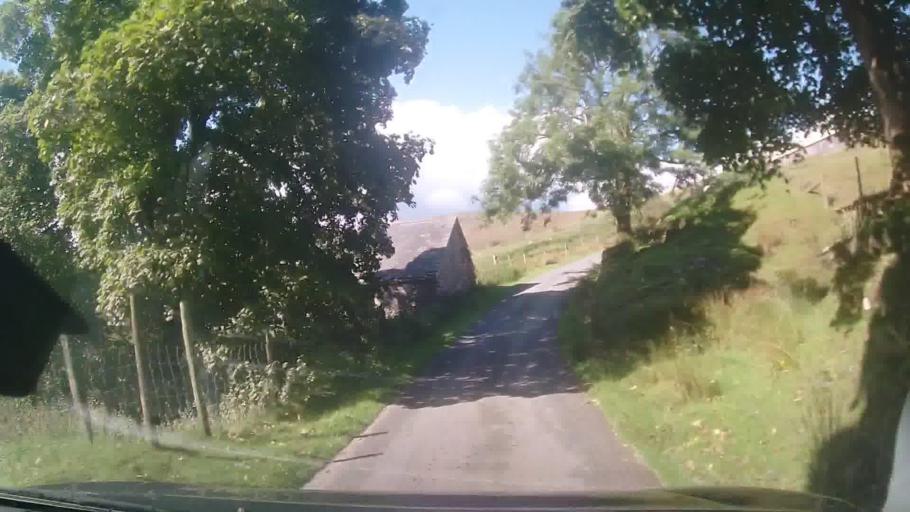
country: GB
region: Wales
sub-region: Gwynedd
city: Bala
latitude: 52.8001
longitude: -3.5755
